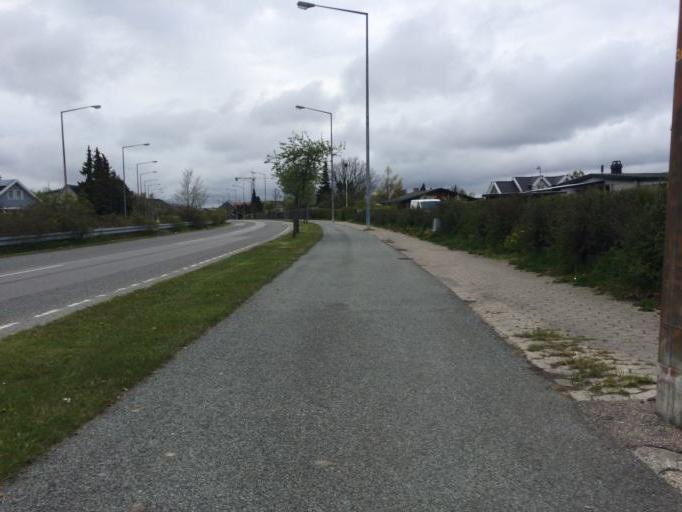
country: DK
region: Capital Region
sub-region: Vallensbaek Kommune
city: Vallensbaek
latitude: 55.6190
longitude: 12.3938
